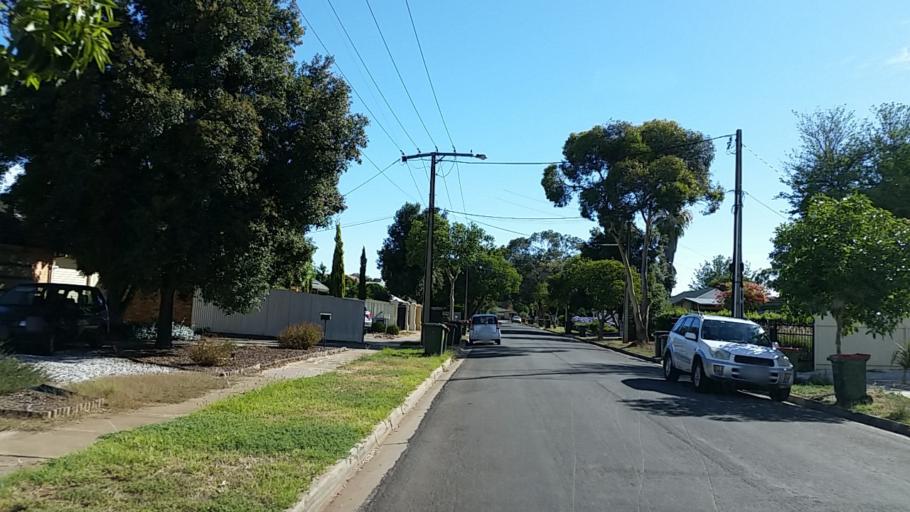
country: AU
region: South Australia
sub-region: Salisbury
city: Salisbury
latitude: -34.7813
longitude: 138.6231
